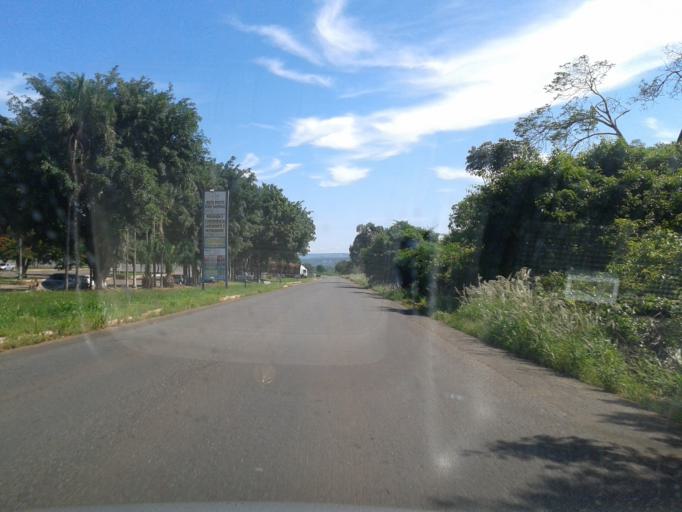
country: BR
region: Goias
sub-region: Piracanjuba
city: Piracanjuba
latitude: -17.2155
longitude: -48.7095
